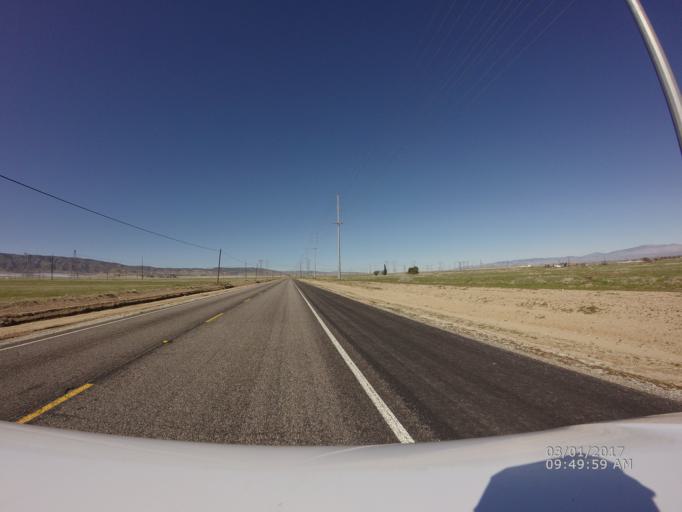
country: US
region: California
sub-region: Los Angeles County
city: Leona Valley
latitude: 34.6747
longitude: -118.2842
